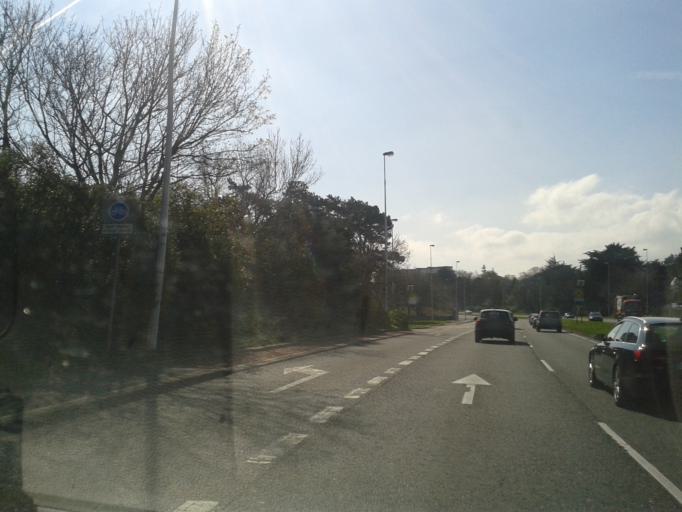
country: IE
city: Booterstown
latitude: 53.2868
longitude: -6.1943
